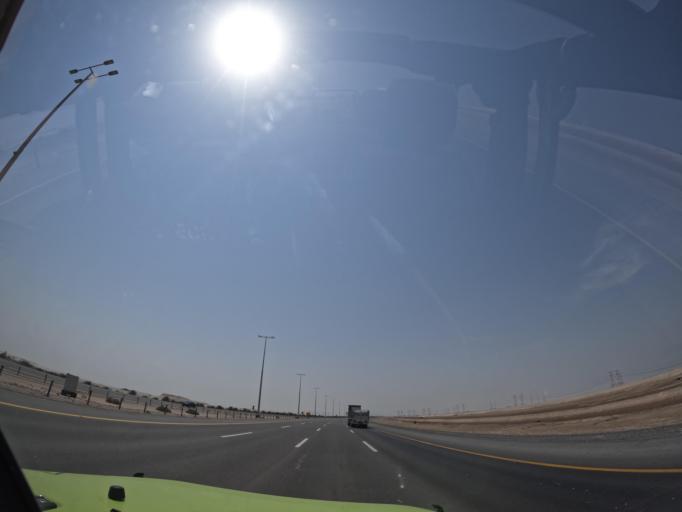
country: AE
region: Abu Dhabi
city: Abu Dhabi
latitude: 24.2324
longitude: 54.4573
